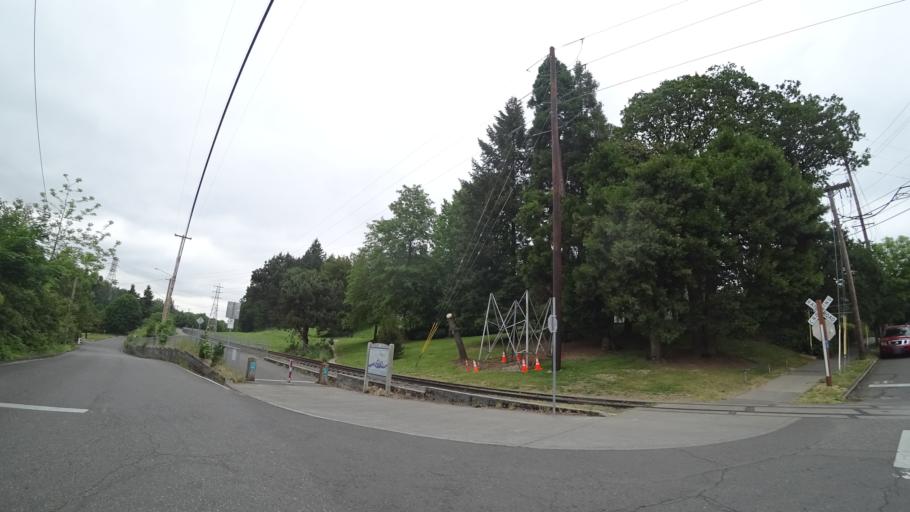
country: US
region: Oregon
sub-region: Clackamas County
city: Milwaukie
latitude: 45.4651
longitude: -122.6619
